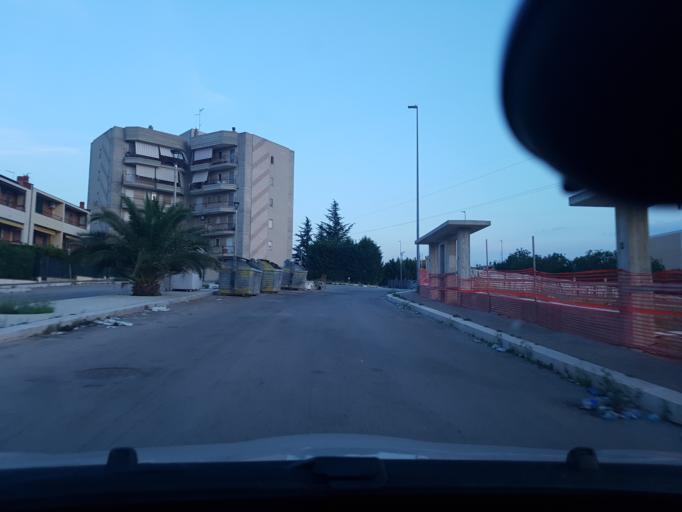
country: IT
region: Apulia
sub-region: Provincia di Foggia
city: Cerignola
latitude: 41.2624
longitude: 15.8779
